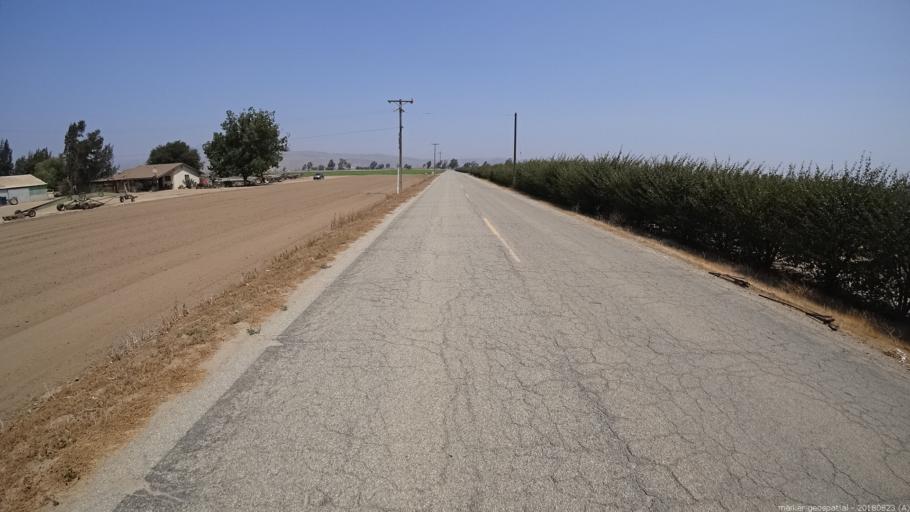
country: US
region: California
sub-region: Monterey County
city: Greenfield
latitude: 36.3357
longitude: -121.2635
